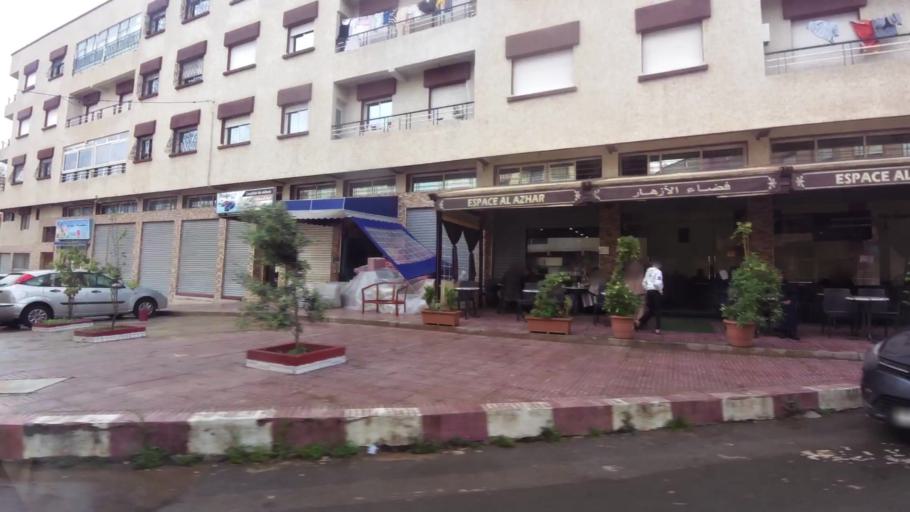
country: MA
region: Grand Casablanca
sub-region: Nouaceur
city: Bouskoura
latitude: 33.5133
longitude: -7.6481
